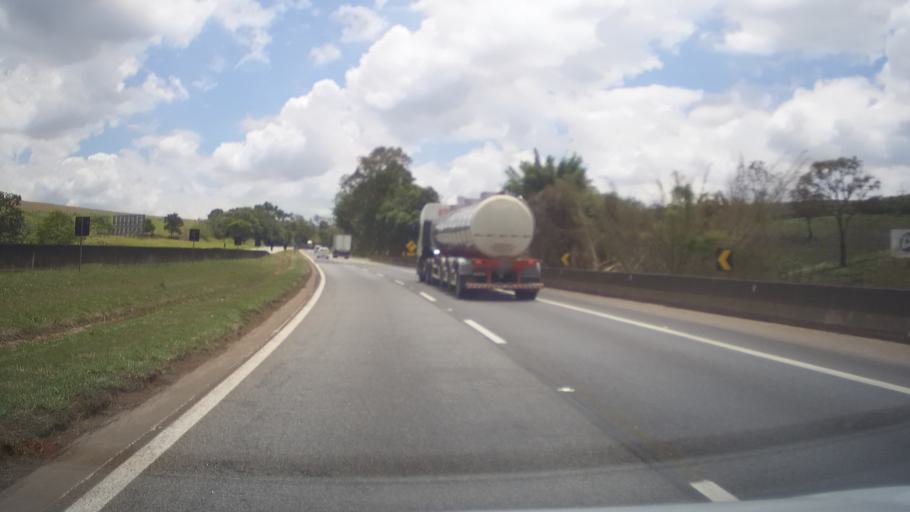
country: BR
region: Minas Gerais
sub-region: Tres Coracoes
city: Tres Coracoes
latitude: -21.7018
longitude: -45.3677
